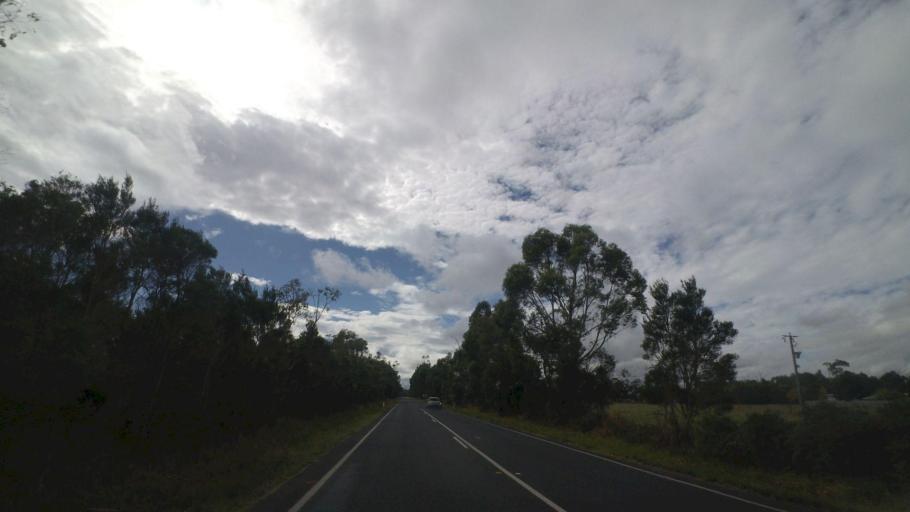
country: AU
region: Victoria
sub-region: Cardinia
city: Bunyip
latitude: -38.0726
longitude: 145.7902
